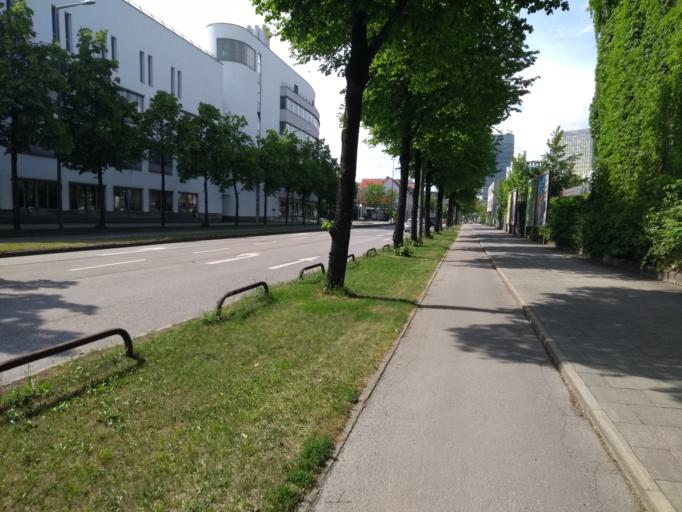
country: DE
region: Bavaria
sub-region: Upper Bavaria
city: Munich
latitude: 48.1292
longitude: 11.5336
